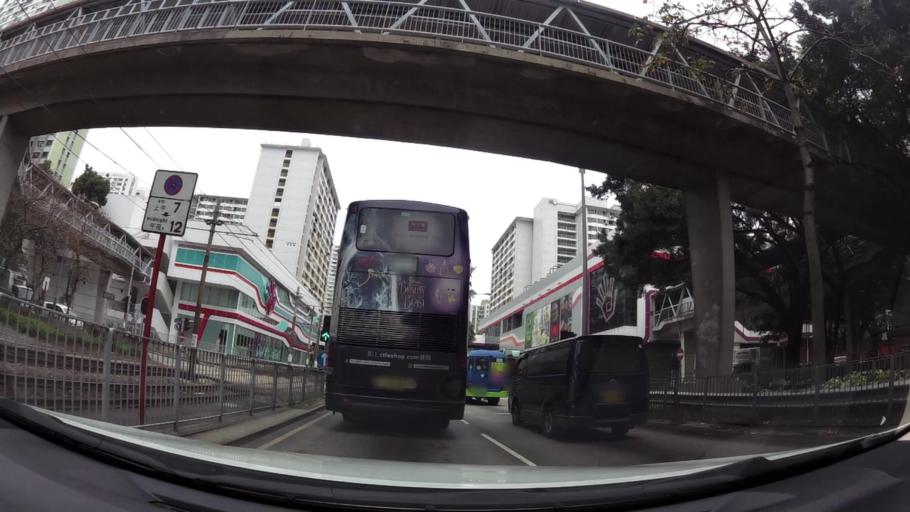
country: HK
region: Tuen Mun
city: Tuen Mun
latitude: 22.3865
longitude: 113.9752
